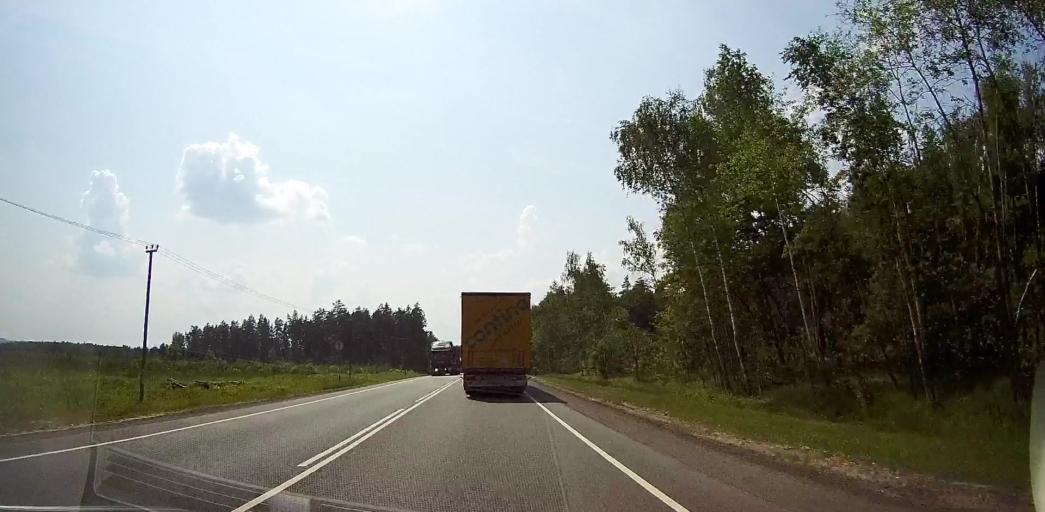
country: RU
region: Moskovskaya
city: Meshcherino
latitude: 55.2057
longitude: 38.3799
